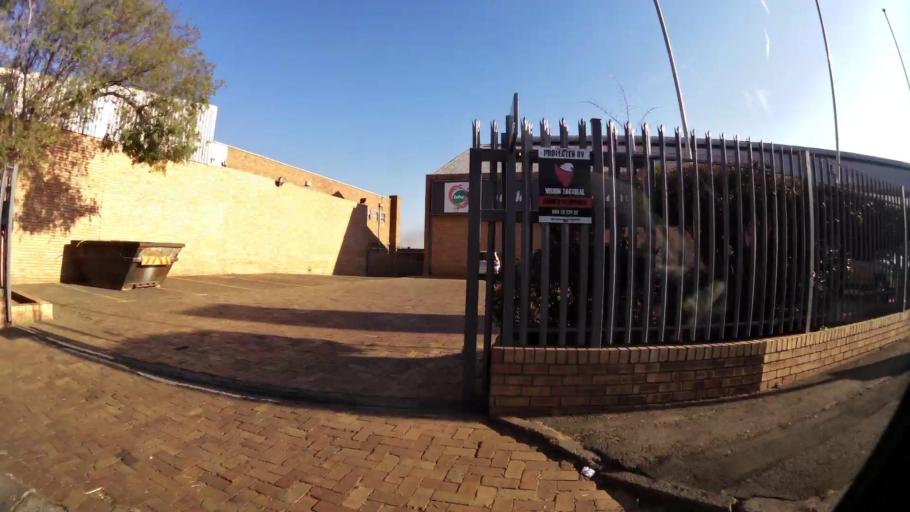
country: ZA
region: Gauteng
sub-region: City of Johannesburg Metropolitan Municipality
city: Johannesburg
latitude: -26.2306
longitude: 28.0278
